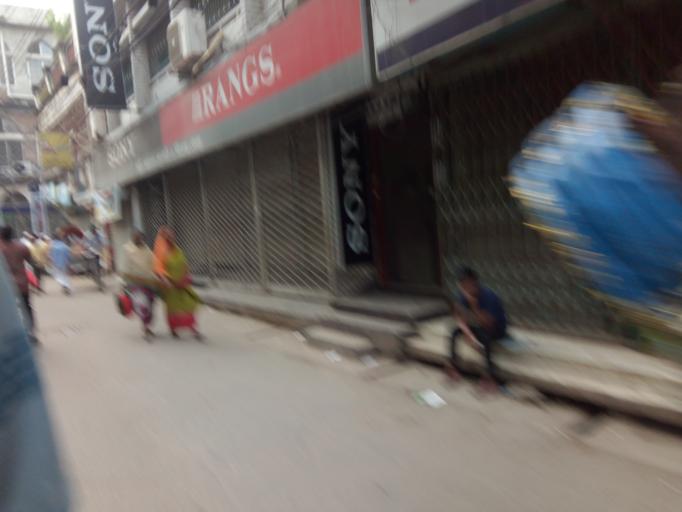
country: BD
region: Dhaka
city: Azimpur
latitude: 23.7191
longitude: 90.3910
